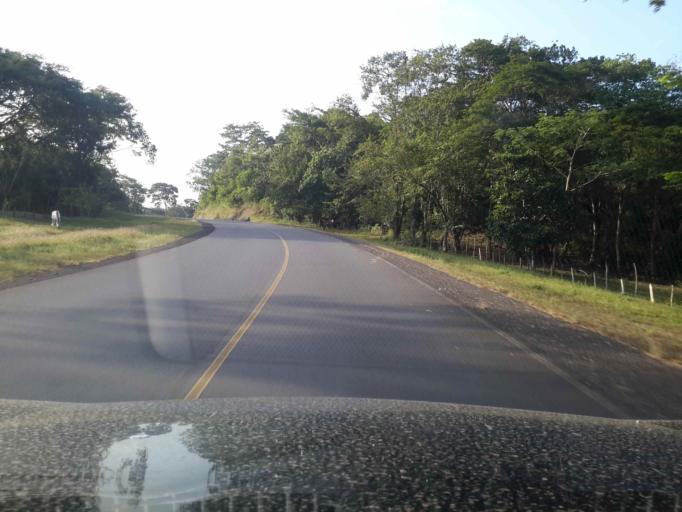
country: NI
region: Rio San Juan
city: San Miguelito
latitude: 11.3819
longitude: -84.7885
